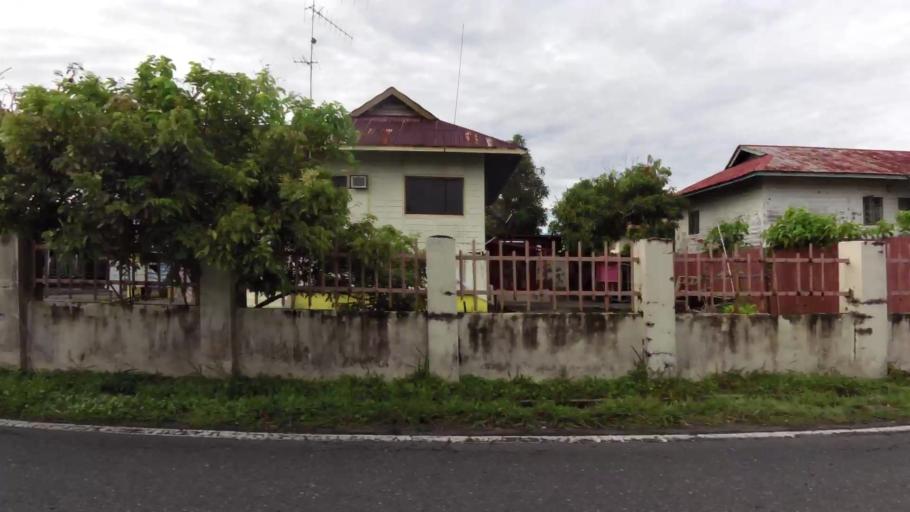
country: BN
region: Belait
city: Seria
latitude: 4.6139
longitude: 114.3275
